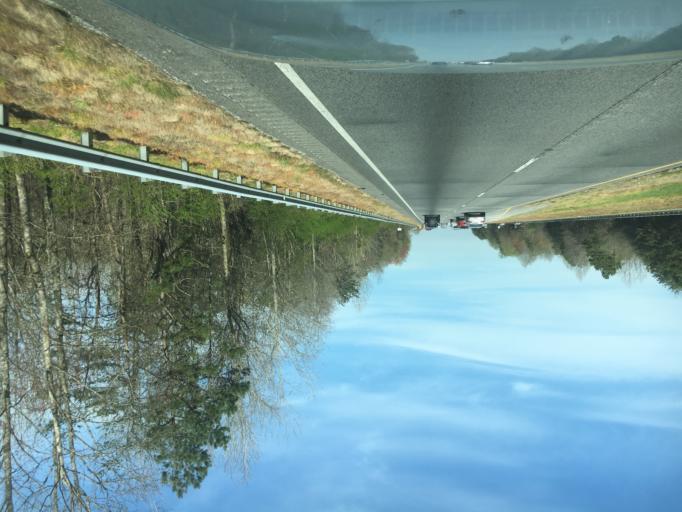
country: US
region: Georgia
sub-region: Hall County
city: Lula
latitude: 34.4057
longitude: -83.6740
